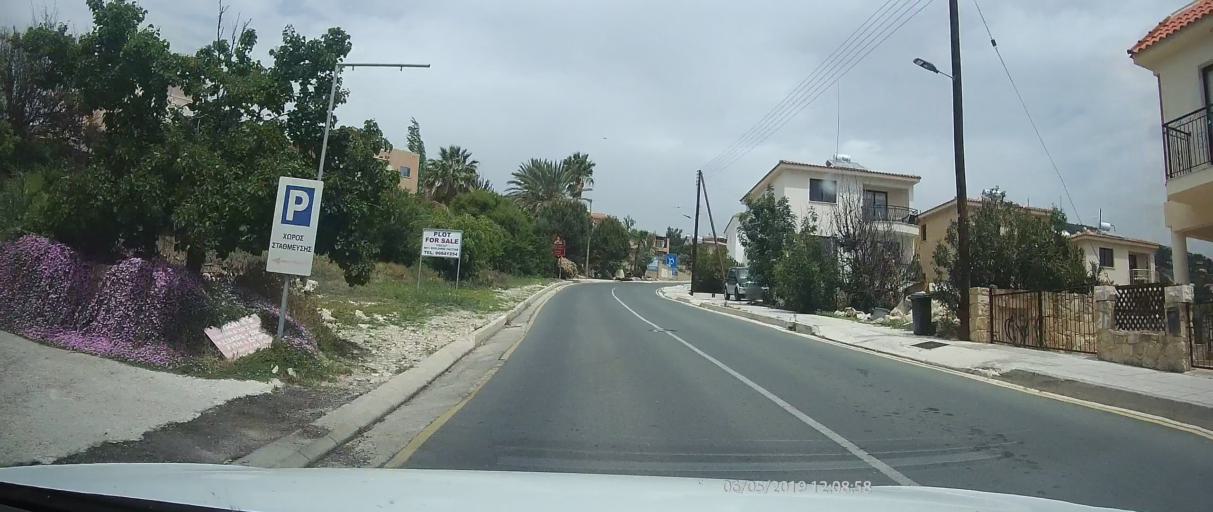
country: CY
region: Pafos
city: Tala
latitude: 34.8371
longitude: 32.4330
